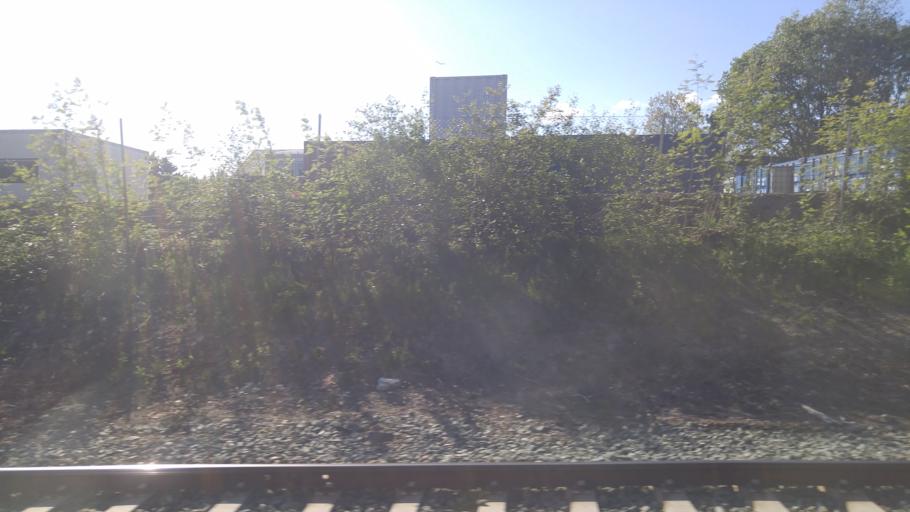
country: NO
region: Sor-Trondelag
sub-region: Trondheim
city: Trondheim
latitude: 63.3488
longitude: 10.3563
